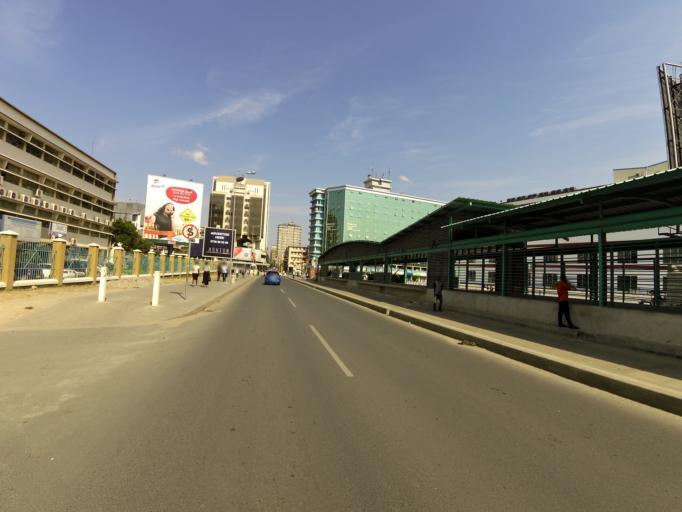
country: TZ
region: Dar es Salaam
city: Dar es Salaam
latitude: -6.8154
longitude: 39.2795
